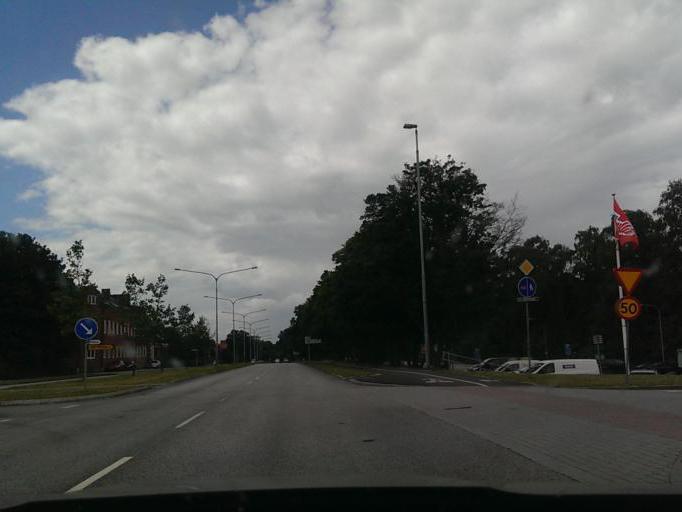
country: SE
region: Skane
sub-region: Lunds Kommun
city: Lund
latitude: 55.7170
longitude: 13.2074
